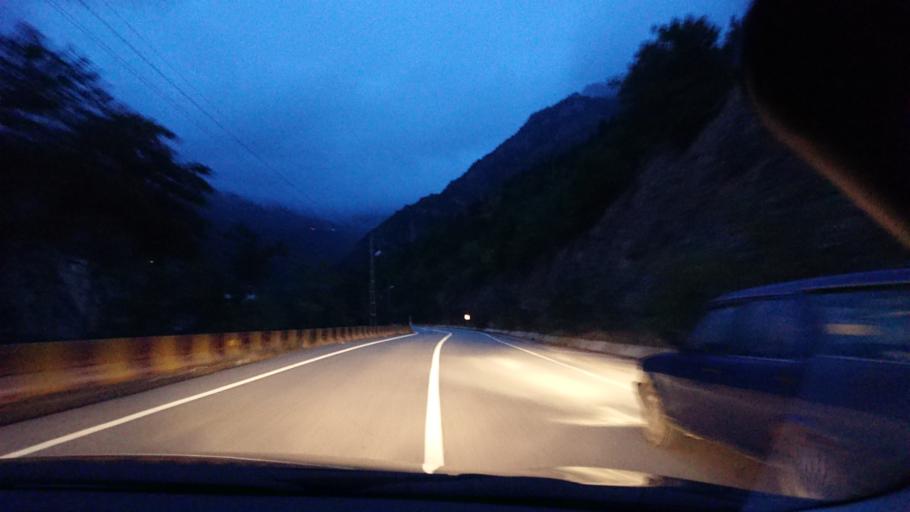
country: TR
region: Gumushane
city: Kurtun
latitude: 40.6742
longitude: 39.1391
